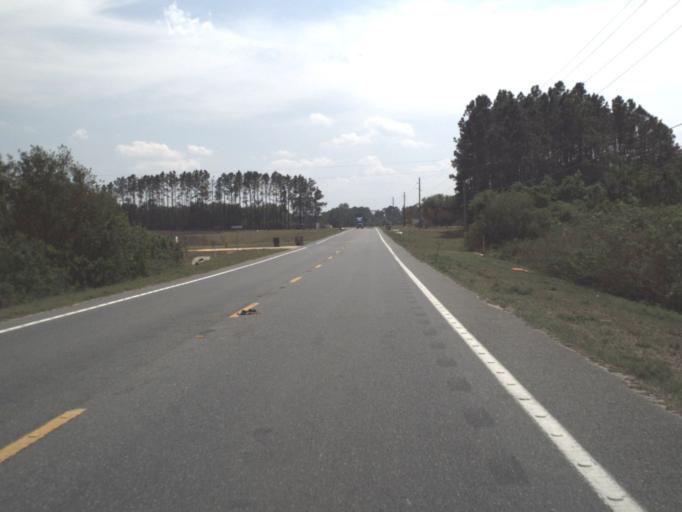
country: US
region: Florida
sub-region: Lake County
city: Howie In The Hills
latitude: 28.6881
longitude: -81.7805
